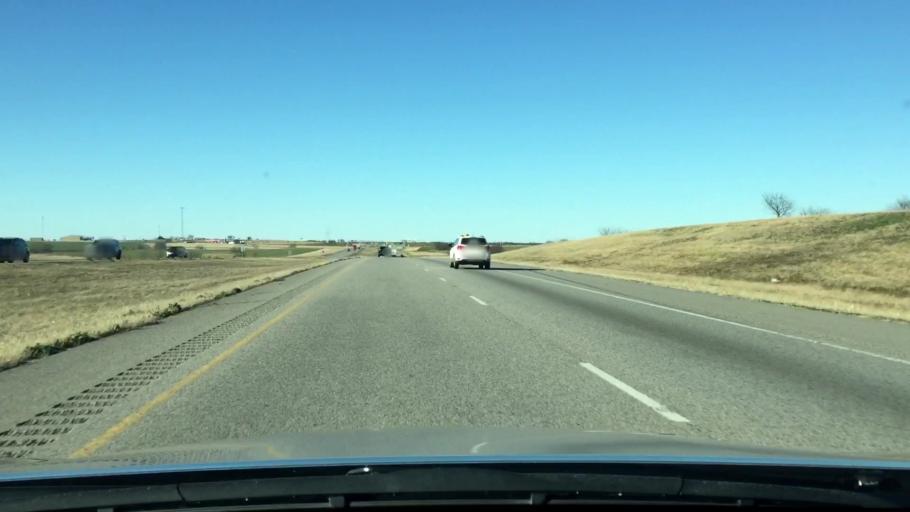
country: US
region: Texas
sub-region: Hill County
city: Itasca
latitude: 32.1419
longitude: -97.1226
